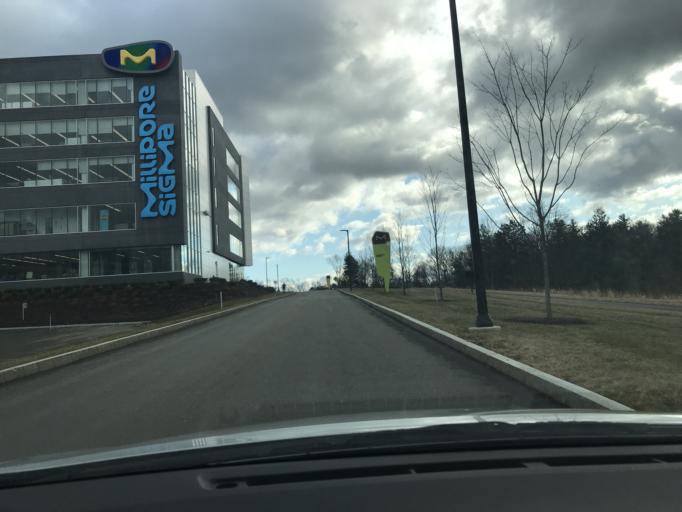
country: US
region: Massachusetts
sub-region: Middlesex County
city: Lexington
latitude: 42.4740
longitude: -71.2172
